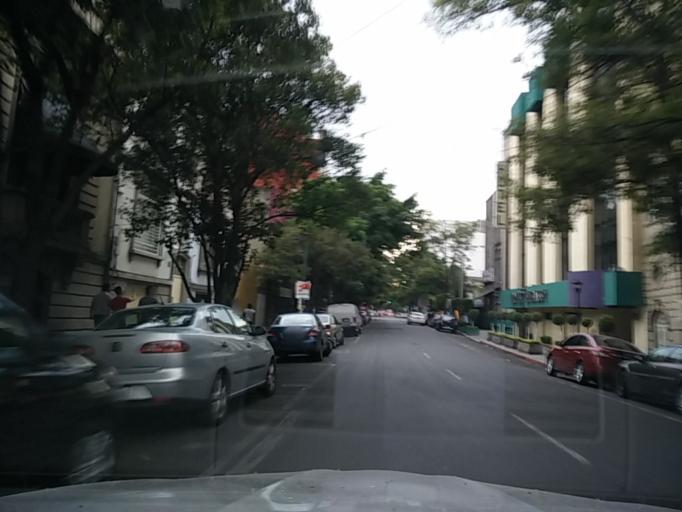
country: MX
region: Mexico City
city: Benito Juarez
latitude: 19.4230
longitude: -99.1598
